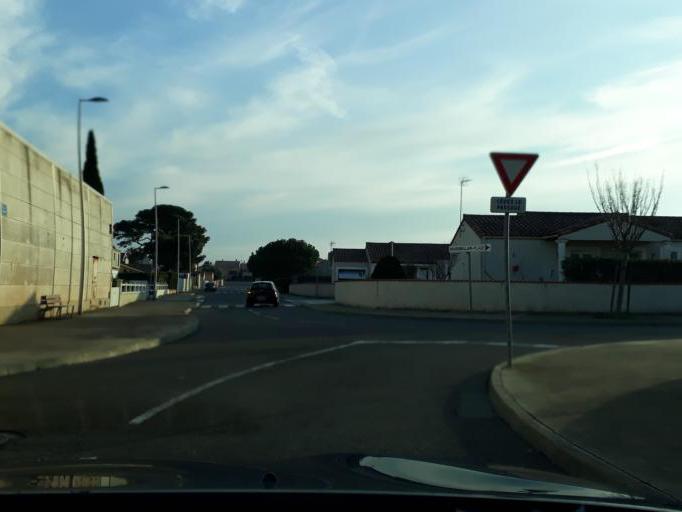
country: FR
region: Languedoc-Roussillon
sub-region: Departement de l'Herault
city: Marseillan
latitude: 43.3520
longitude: 3.5301
